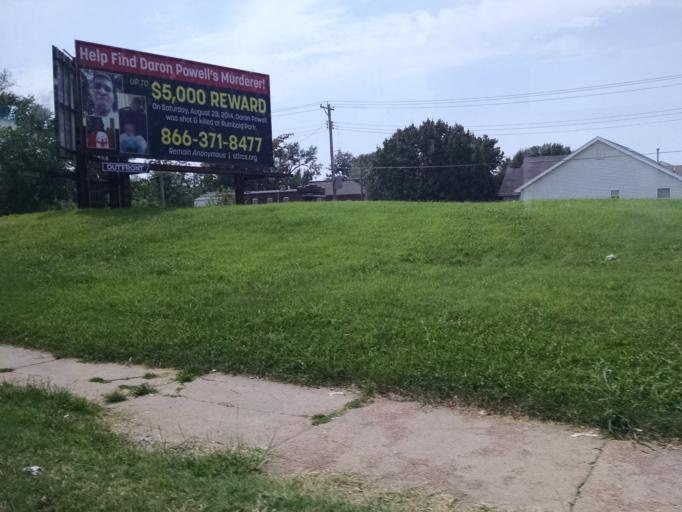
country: US
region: Missouri
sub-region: City of Saint Louis
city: St. Louis
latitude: 38.6501
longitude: -90.2247
